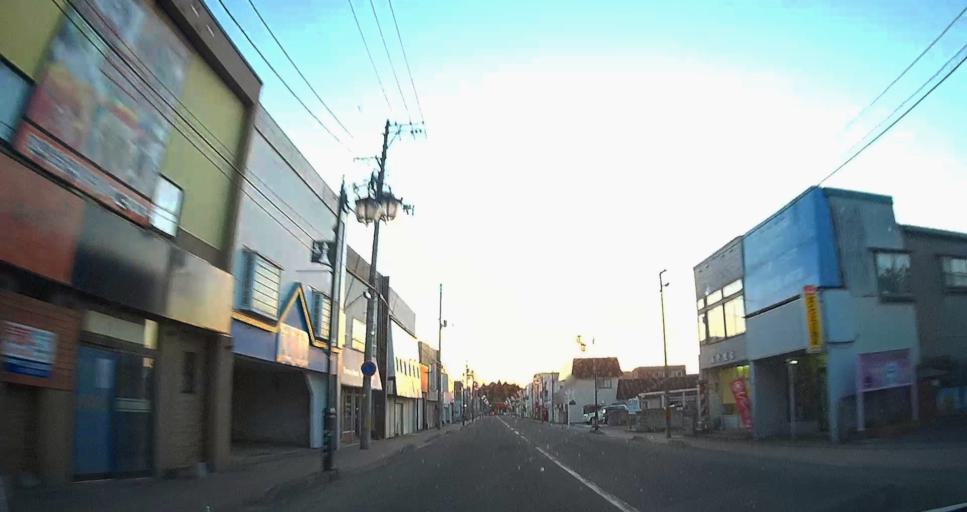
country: JP
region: Aomori
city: Misawa
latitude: 40.8669
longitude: 141.1263
